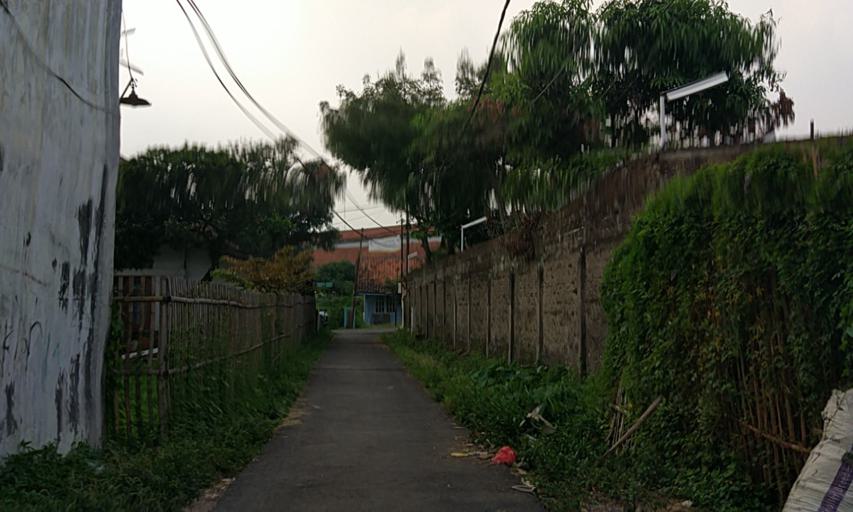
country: ID
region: West Java
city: Bandung
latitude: -6.9076
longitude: 107.6746
